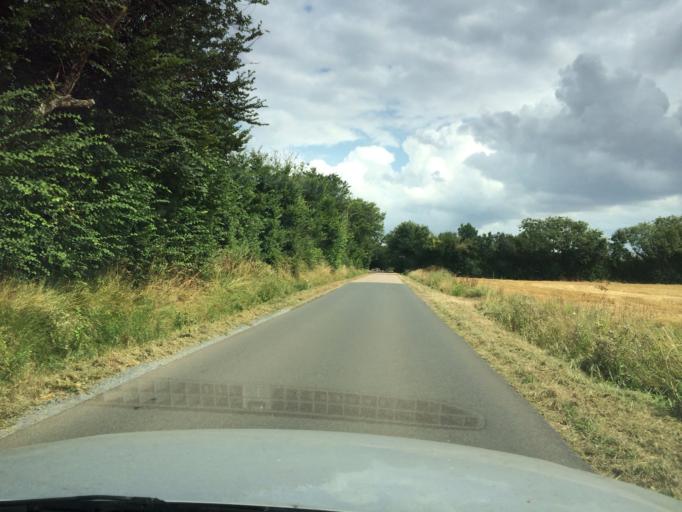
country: FR
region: Lower Normandy
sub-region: Departement du Calvados
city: Bayeux
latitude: 49.3008
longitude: -0.7254
